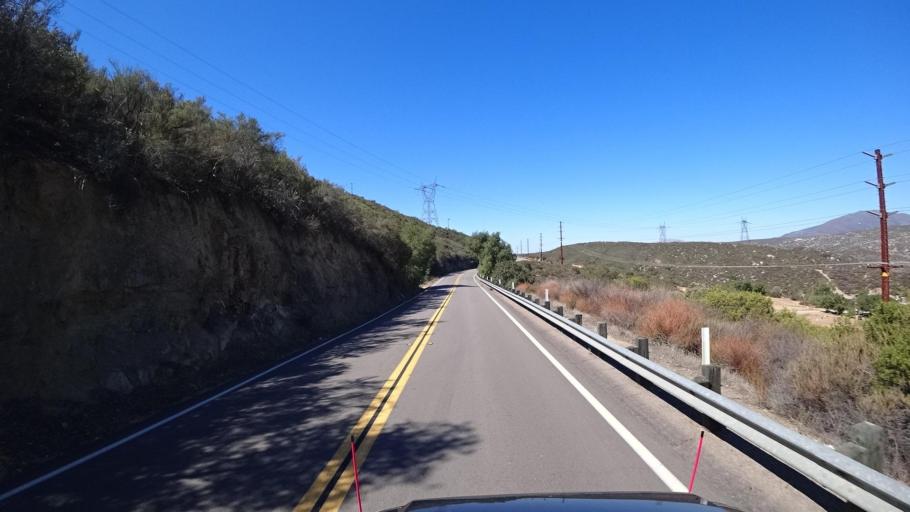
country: US
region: California
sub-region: San Diego County
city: Alpine
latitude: 32.7757
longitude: -116.7102
